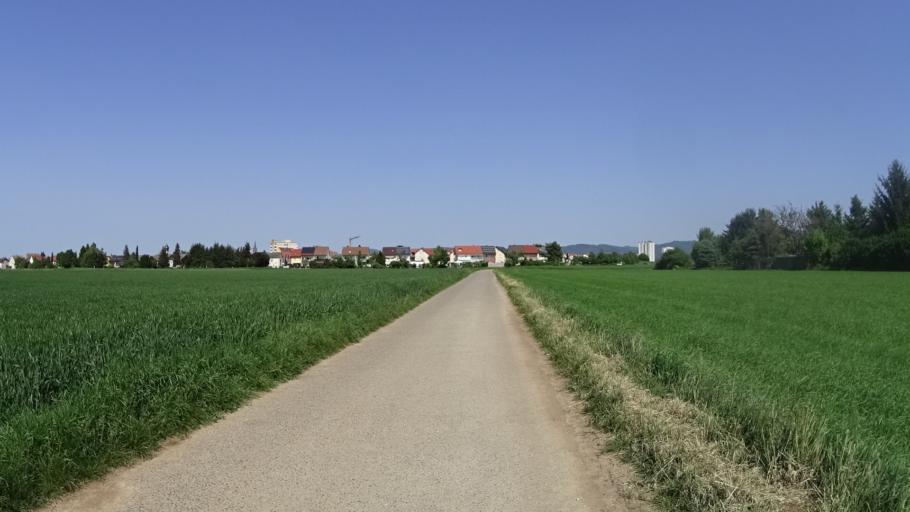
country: DE
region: Baden-Wuerttemberg
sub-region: Karlsruhe Region
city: Heddesheim
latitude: 49.4996
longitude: 8.5962
